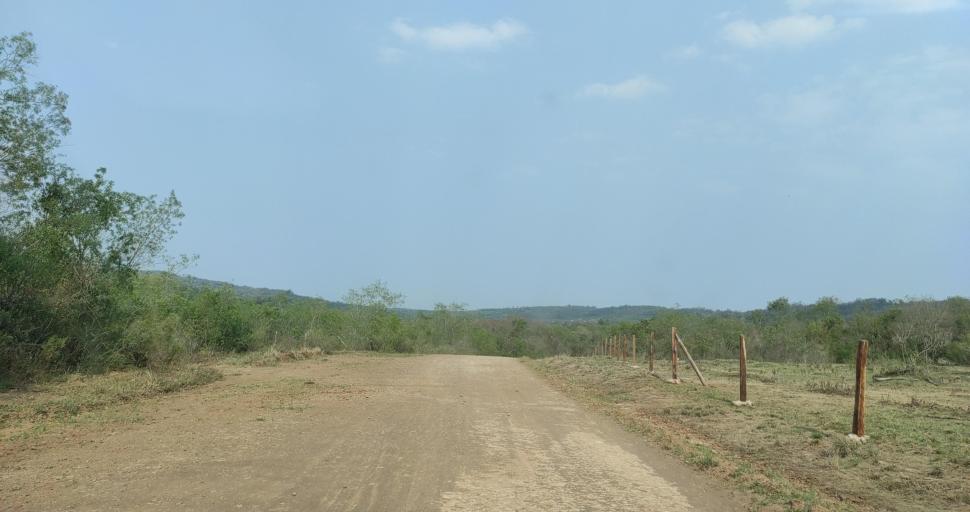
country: AR
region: Misiones
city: Cerro Azul
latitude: -27.6006
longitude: -55.5735
